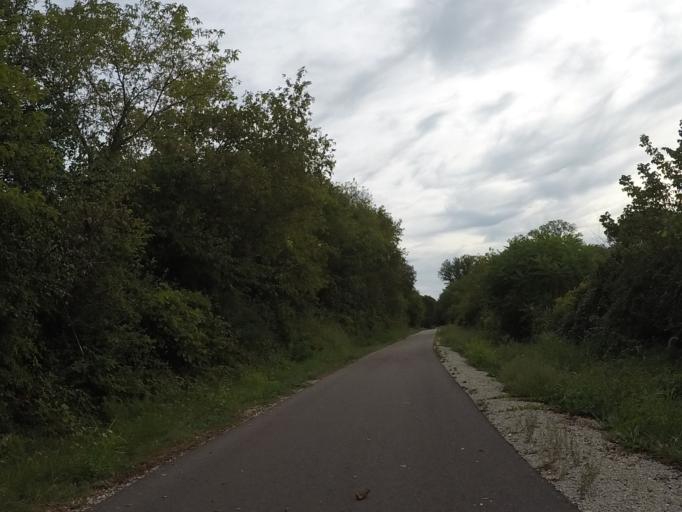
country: US
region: Wisconsin
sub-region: Sauk County
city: Baraboo
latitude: 43.3810
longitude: -89.7331
